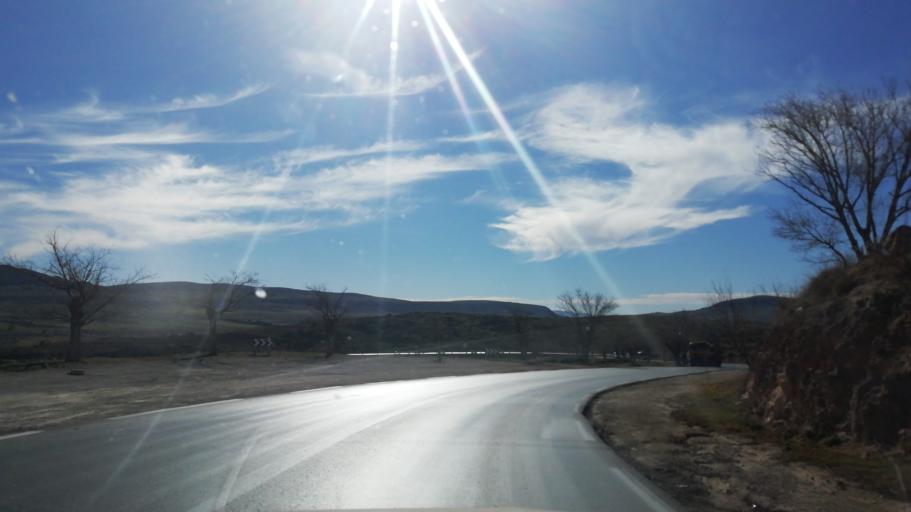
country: DZ
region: Tlemcen
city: Mansoura
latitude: 34.8230
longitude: -1.3697
